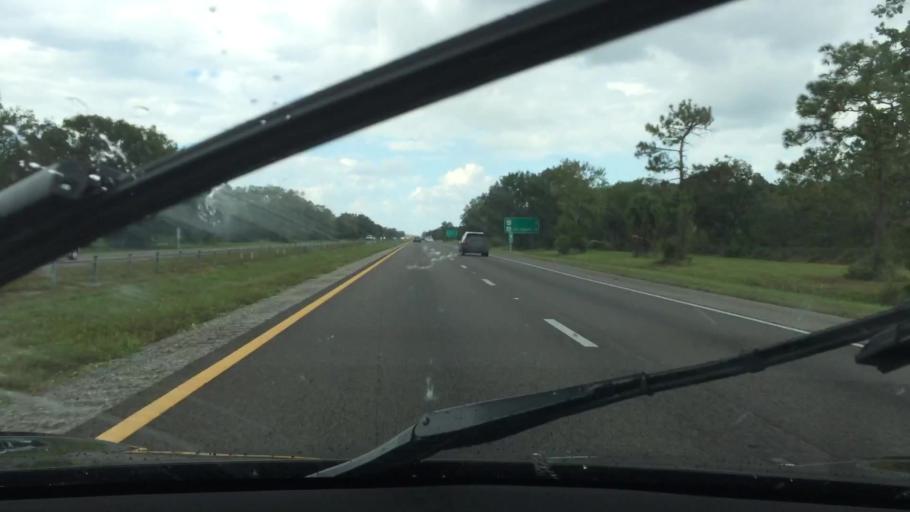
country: US
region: Florida
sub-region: Orange County
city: Wedgefield
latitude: 28.4517
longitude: -81.0762
